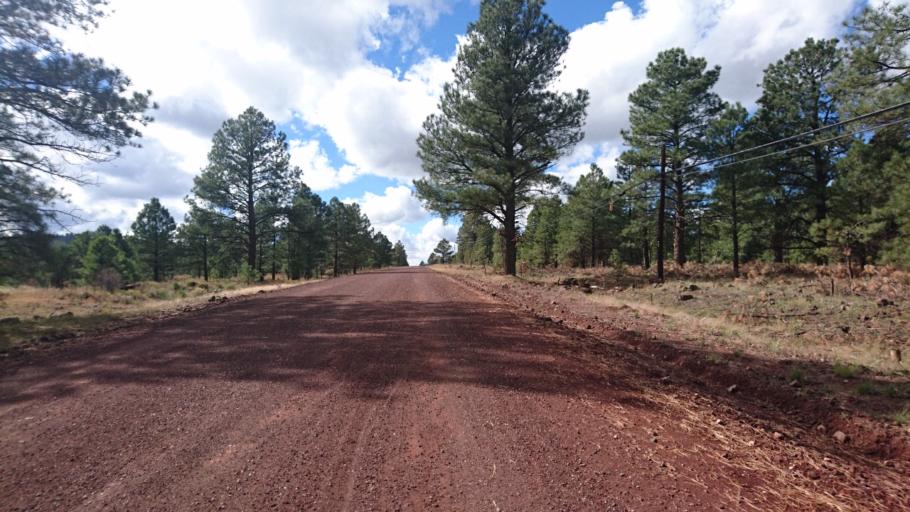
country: US
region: Arizona
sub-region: Coconino County
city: Williams
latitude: 35.2649
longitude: -112.0881
